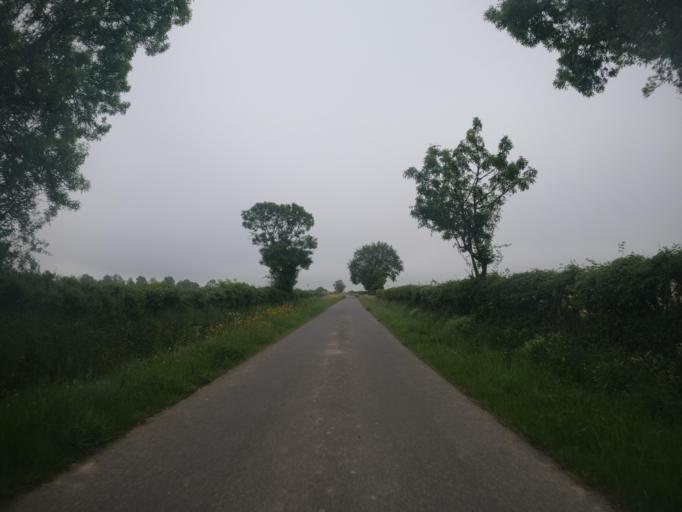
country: FR
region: Poitou-Charentes
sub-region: Departement des Deux-Sevres
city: Mauze-Thouarsais
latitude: 46.9037
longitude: -0.3299
